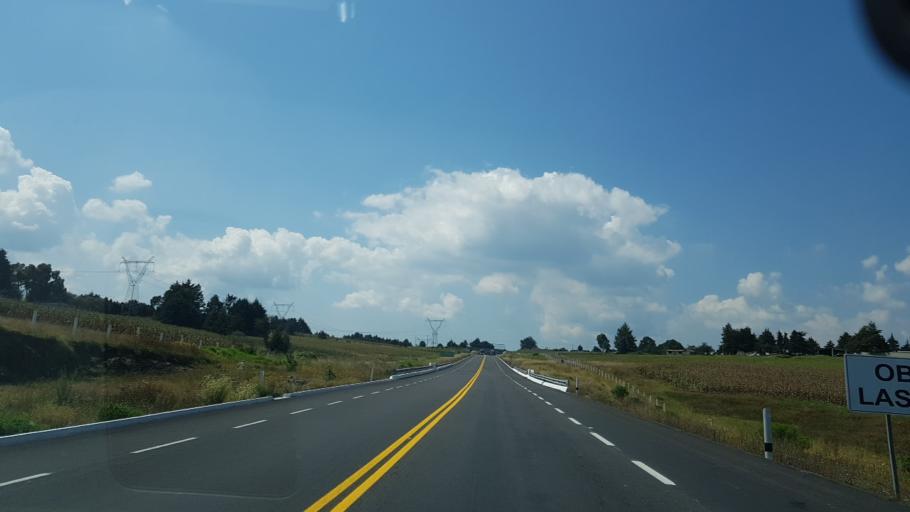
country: MX
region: Mexico
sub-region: Villa Victoria
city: Colonia Doctor Gustavo Baz
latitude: 19.3762
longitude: -99.9070
